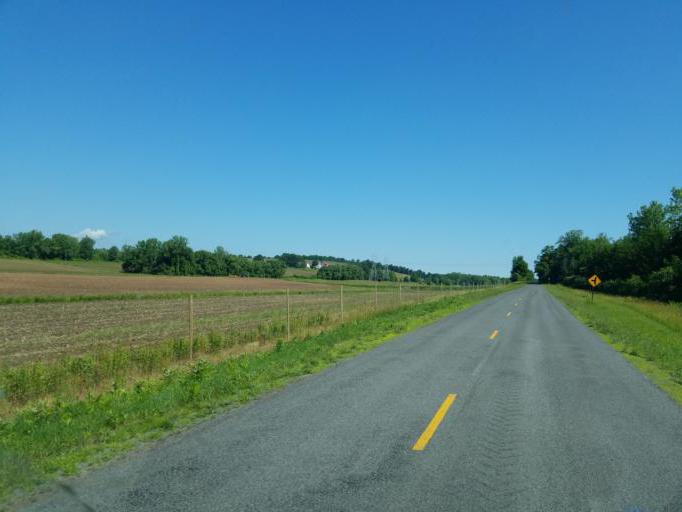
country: US
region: New York
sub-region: Wayne County
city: Clyde
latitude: 43.1295
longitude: -76.8416
